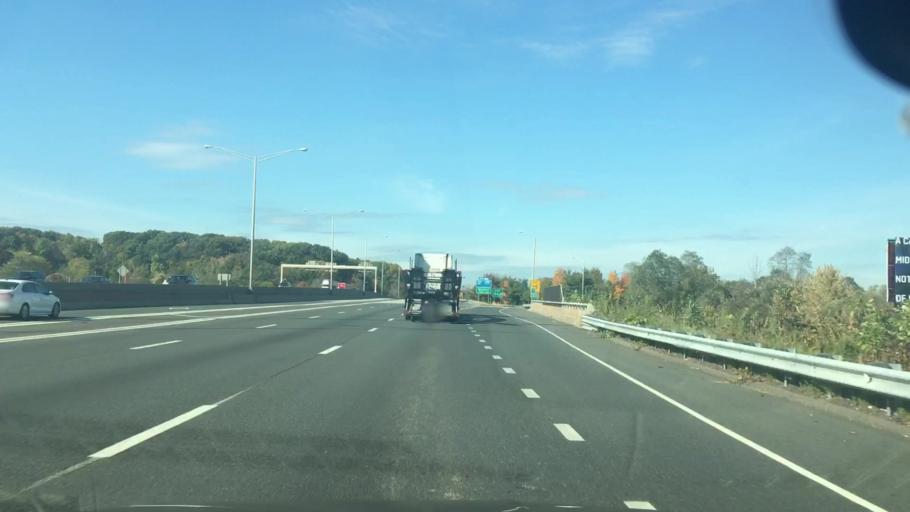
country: US
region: Connecticut
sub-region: Hartford County
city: South Windsor
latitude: 41.8023
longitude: -72.6565
